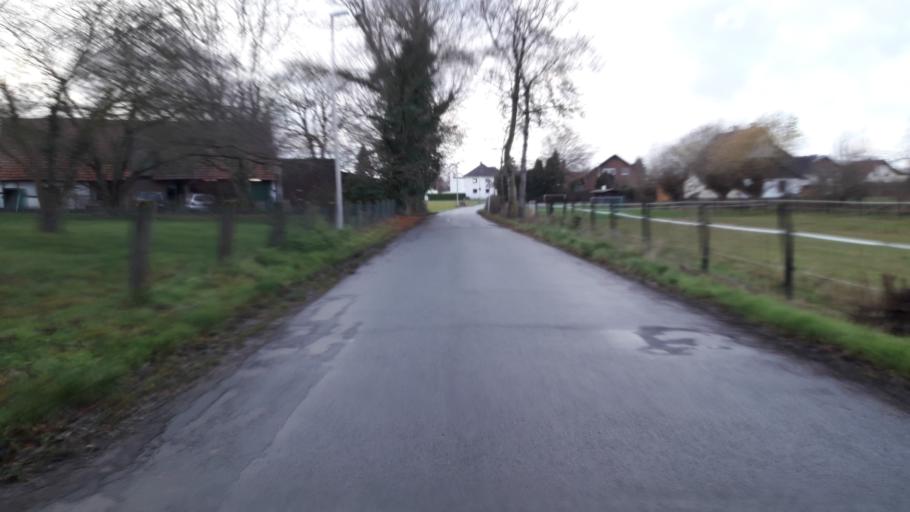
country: DE
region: North Rhine-Westphalia
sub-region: Regierungsbezirk Detmold
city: Minden
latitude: 52.3106
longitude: 8.9543
